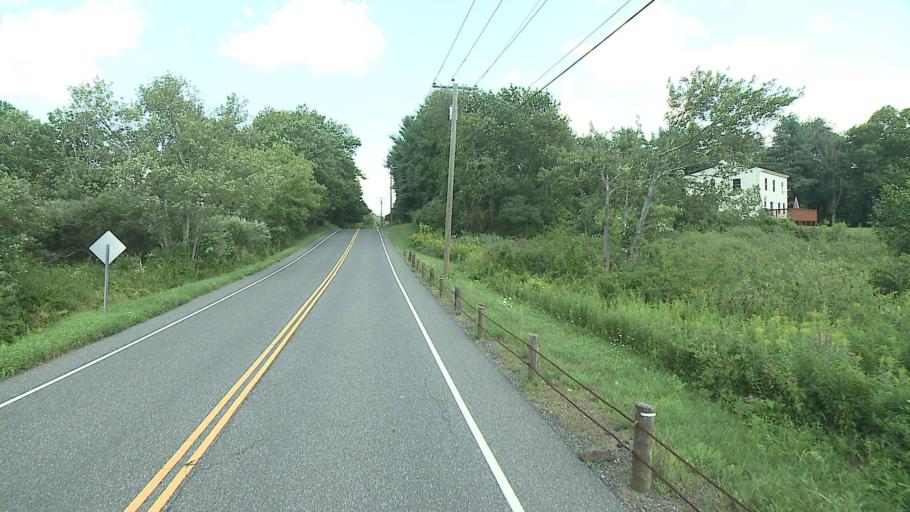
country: US
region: Connecticut
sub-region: Litchfield County
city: Bethlehem Village
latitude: 41.6802
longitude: -73.2413
